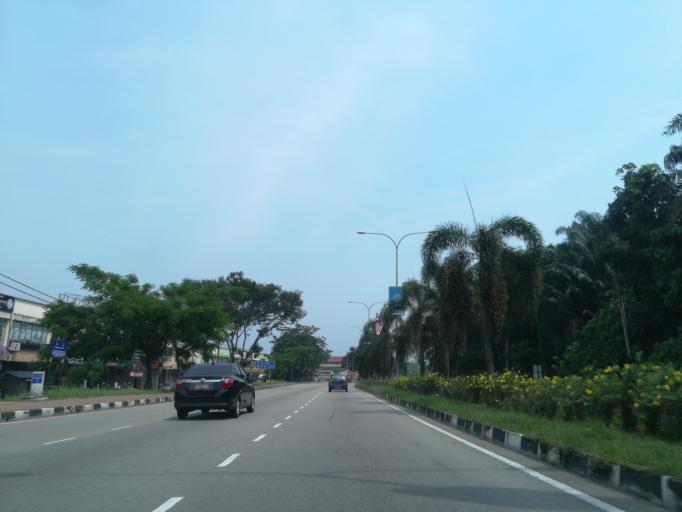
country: MY
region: Kedah
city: Kulim
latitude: 5.4129
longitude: 100.5430
